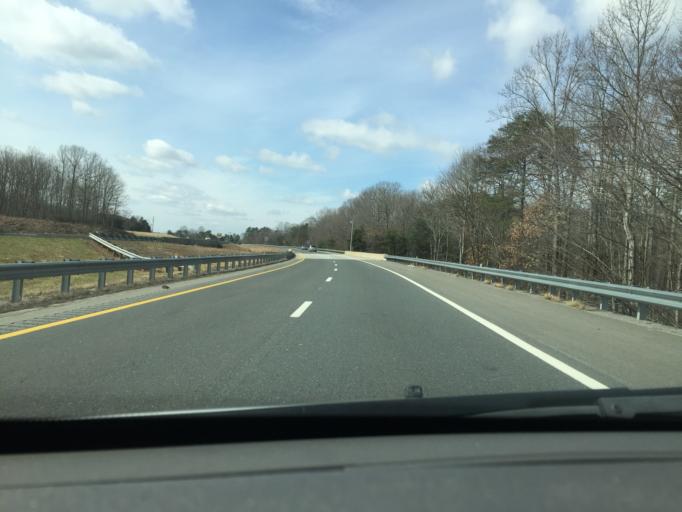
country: US
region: Virginia
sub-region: Campbell County
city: Timberlake
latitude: 37.3106
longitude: -79.2613
